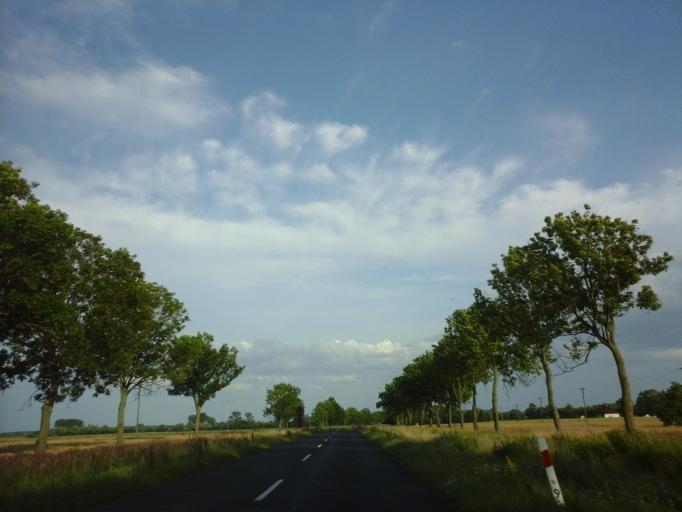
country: PL
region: West Pomeranian Voivodeship
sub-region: Powiat kamienski
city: Kamien Pomorski
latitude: 53.9506
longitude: 14.7993
